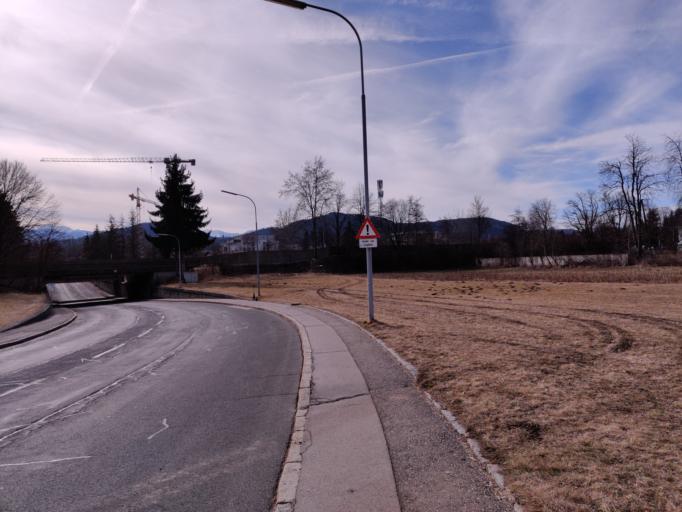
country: AT
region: Carinthia
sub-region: Klagenfurt am Woerthersee
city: Klagenfurt am Woerthersee
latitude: 46.6240
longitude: 14.2696
